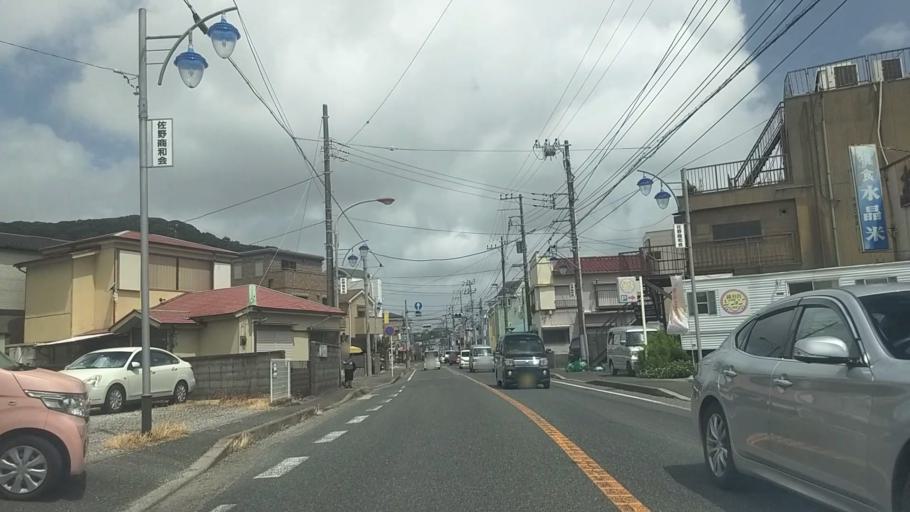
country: JP
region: Kanagawa
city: Yokosuka
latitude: 35.2603
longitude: 139.6687
